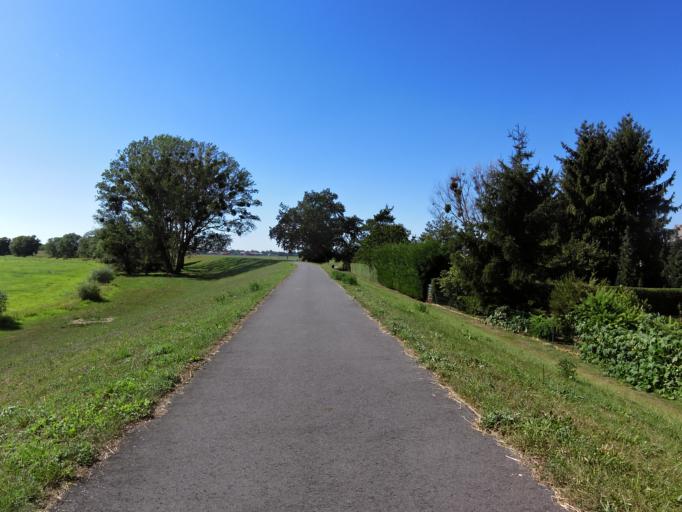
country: DE
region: Saxony-Anhalt
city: Muhlanger
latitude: 51.8381
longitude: 12.7830
